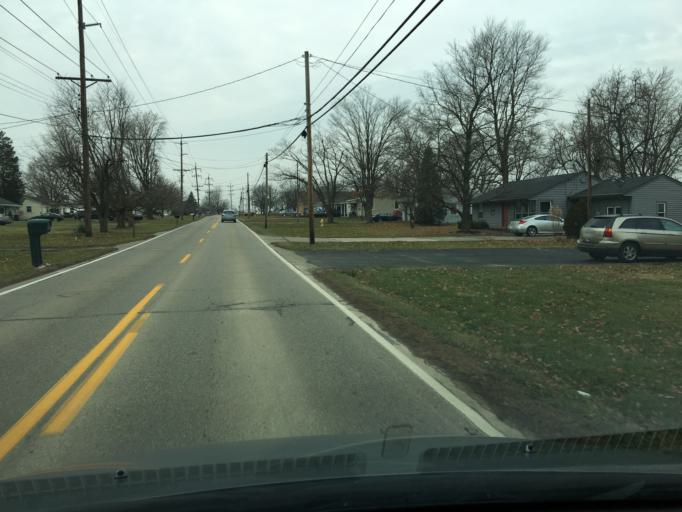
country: US
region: Ohio
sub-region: Hamilton County
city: Highpoint
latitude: 39.3178
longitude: -84.3628
